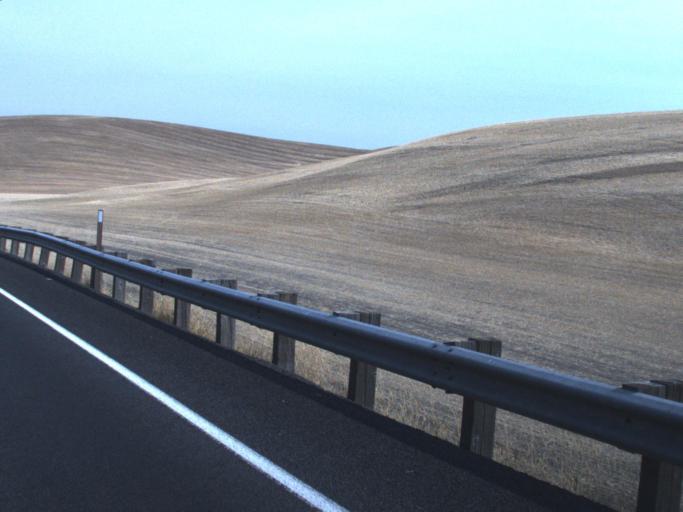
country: US
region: Washington
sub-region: Whitman County
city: Pullman
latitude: 46.7799
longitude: -117.1517
